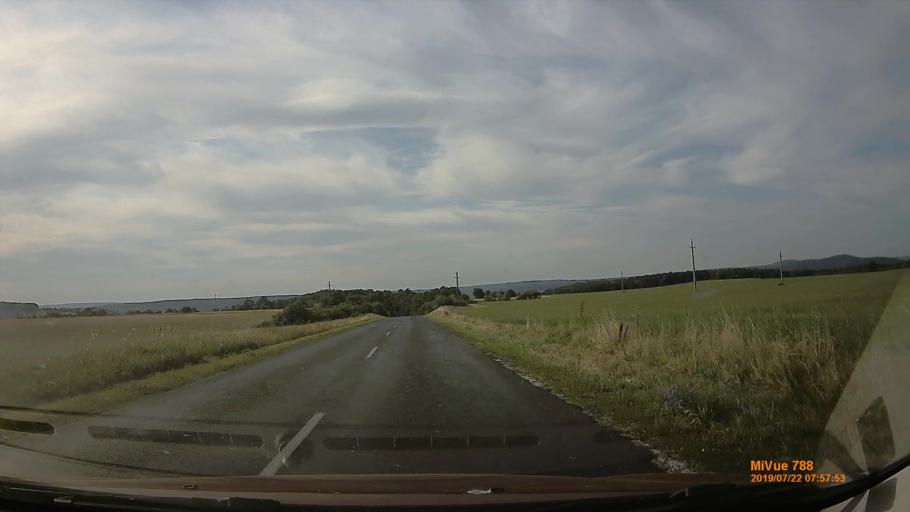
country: HU
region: Veszprem
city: Urkut
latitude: 47.0127
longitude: 17.5895
